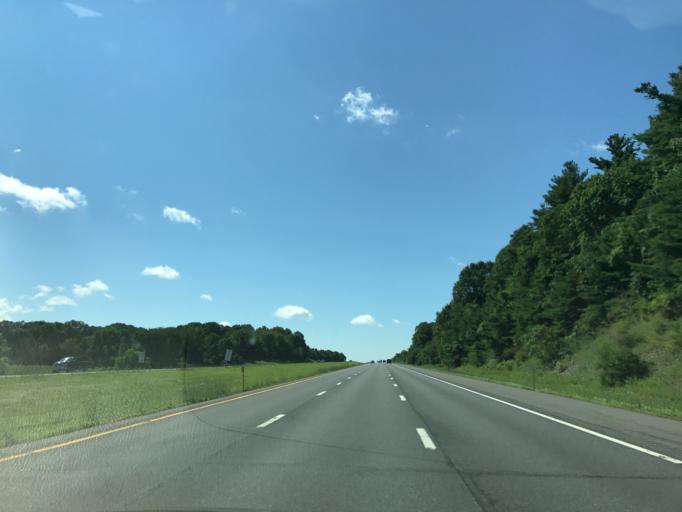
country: US
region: New York
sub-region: Rensselaer County
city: East Greenbush
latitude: 42.6115
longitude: -73.6874
